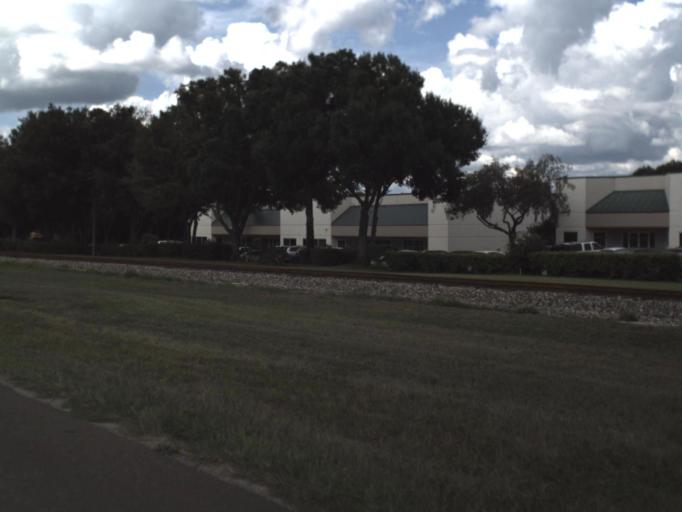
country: US
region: Florida
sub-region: Polk County
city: Crystal Lake
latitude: 28.0283
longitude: -81.9295
